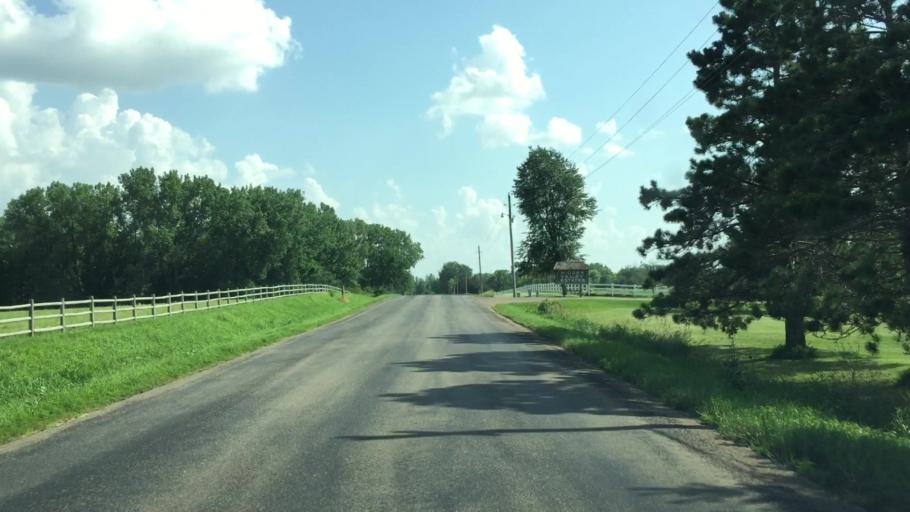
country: US
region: Iowa
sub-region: Johnson County
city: North Liberty
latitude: 41.8107
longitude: -91.6149
